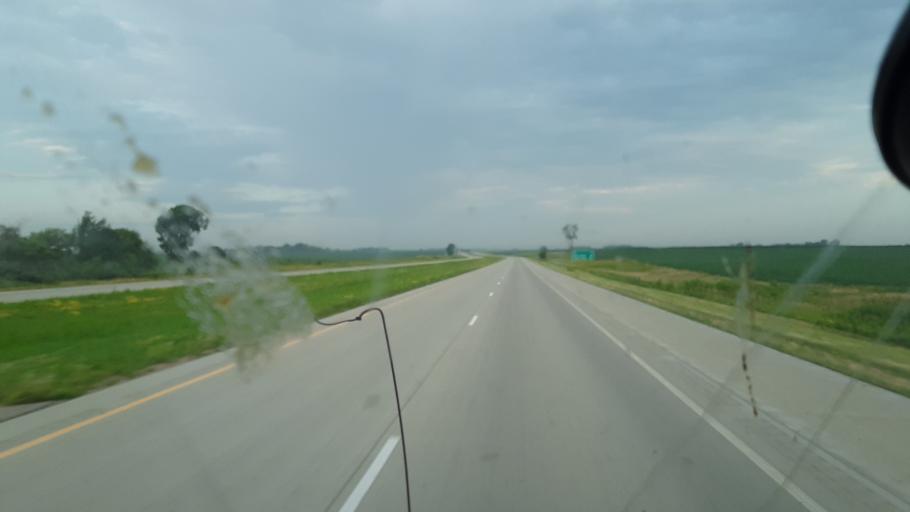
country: US
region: Minnesota
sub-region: Faribault County
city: Wells
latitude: 43.6665
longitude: -93.5922
